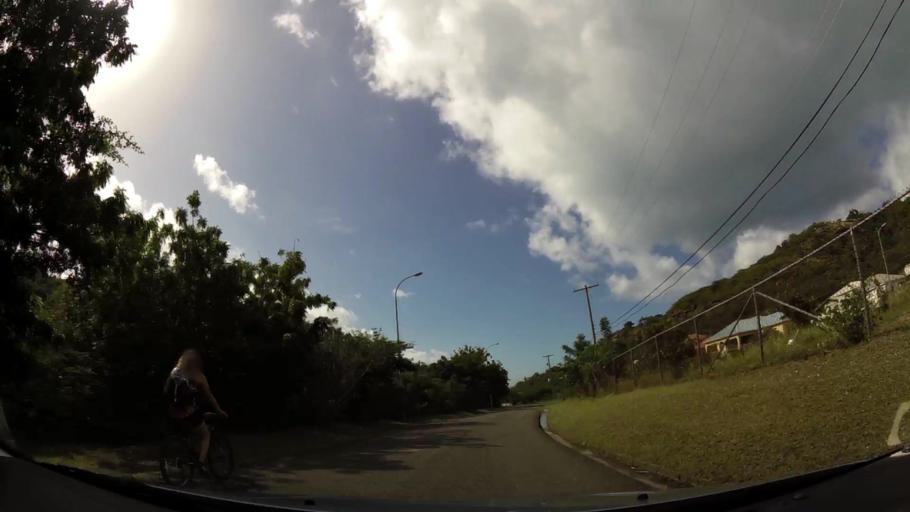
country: AG
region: Saint John
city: Saint John's
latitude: 17.1191
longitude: -61.8844
